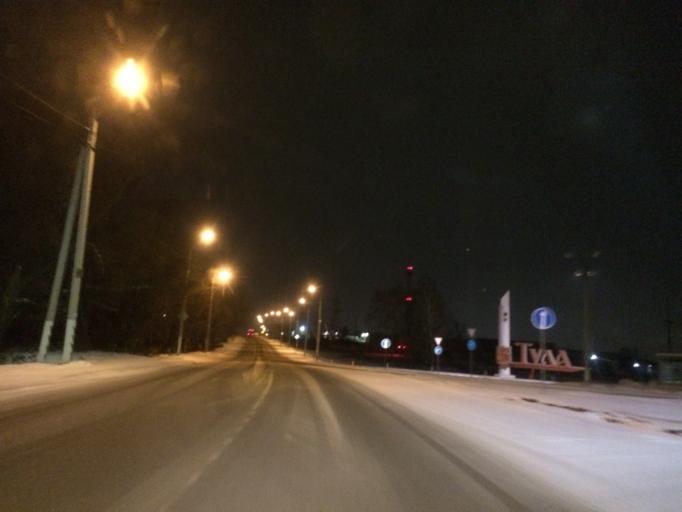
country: RU
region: Tula
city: Gorelki
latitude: 54.2361
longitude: 37.6567
